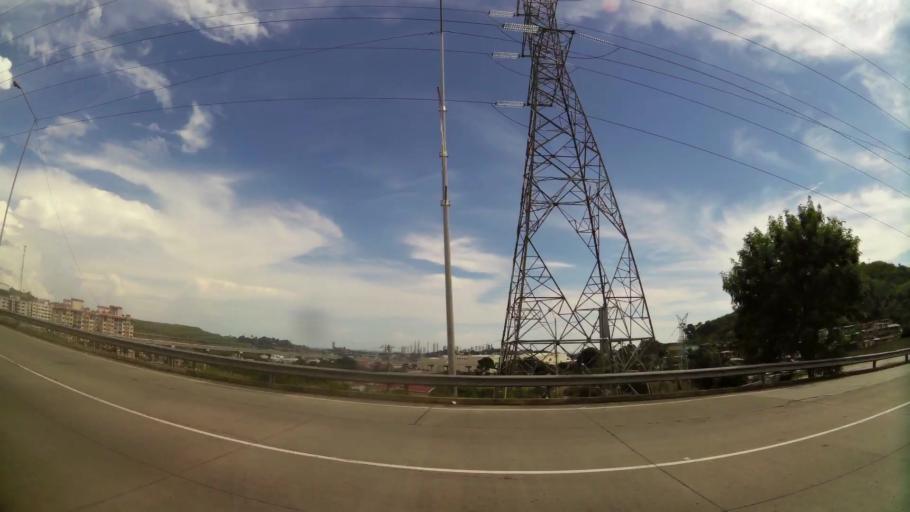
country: PA
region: Panama
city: Las Cumbres
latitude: 9.0577
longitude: -79.5118
